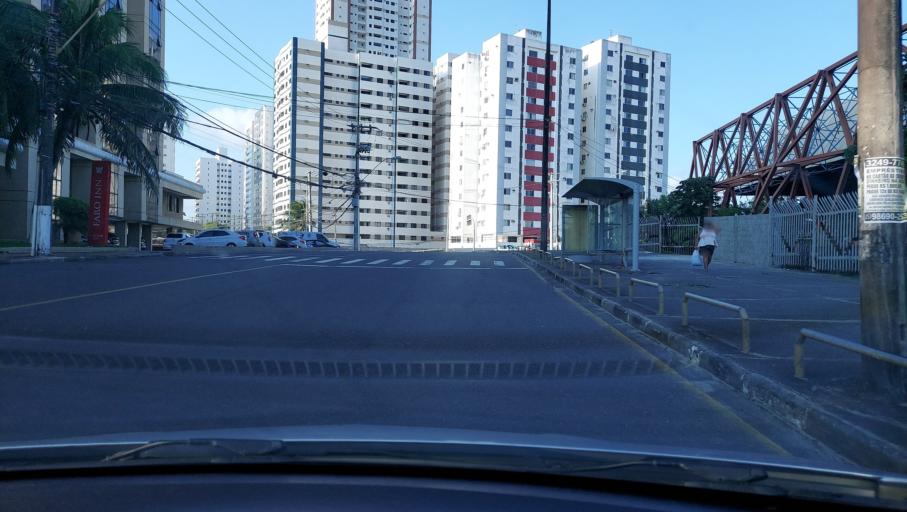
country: BR
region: Bahia
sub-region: Salvador
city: Salvador
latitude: -12.9825
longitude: -38.4414
